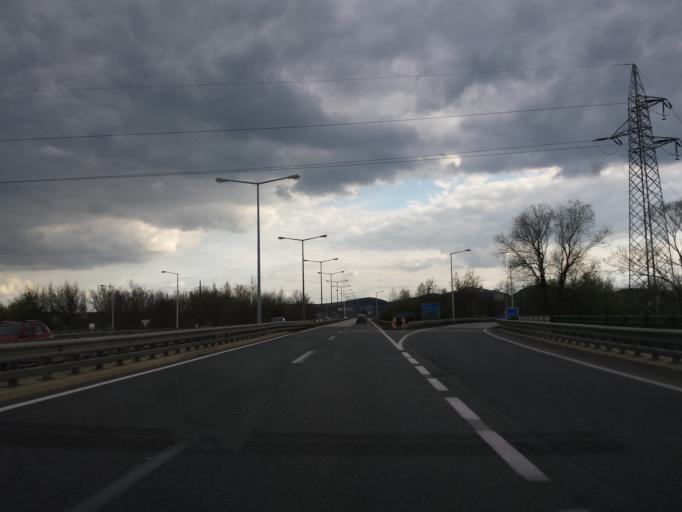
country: AT
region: Lower Austria
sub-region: Krems an der Donau Stadt
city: Krems an der Donau
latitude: 48.4104
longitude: 15.6250
